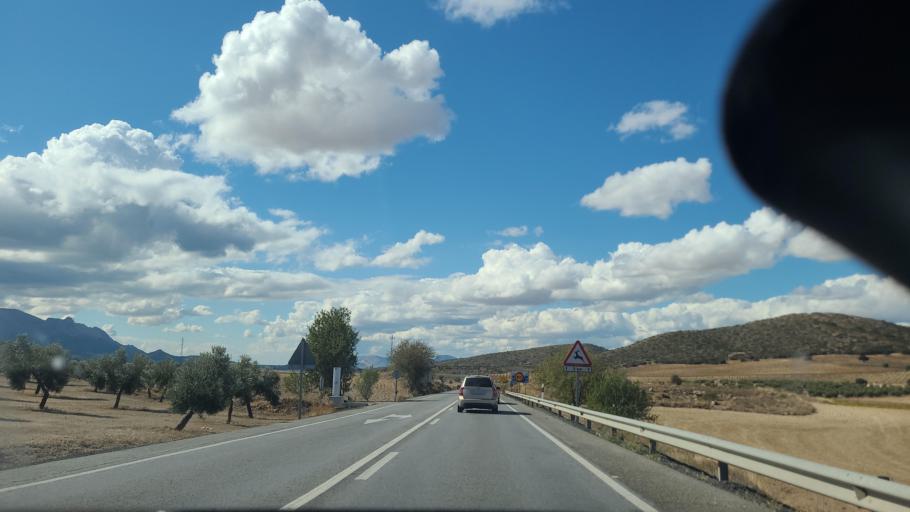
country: ES
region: Andalusia
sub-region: Provincia de Granada
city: Pinar
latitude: 37.4061
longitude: -3.3820
